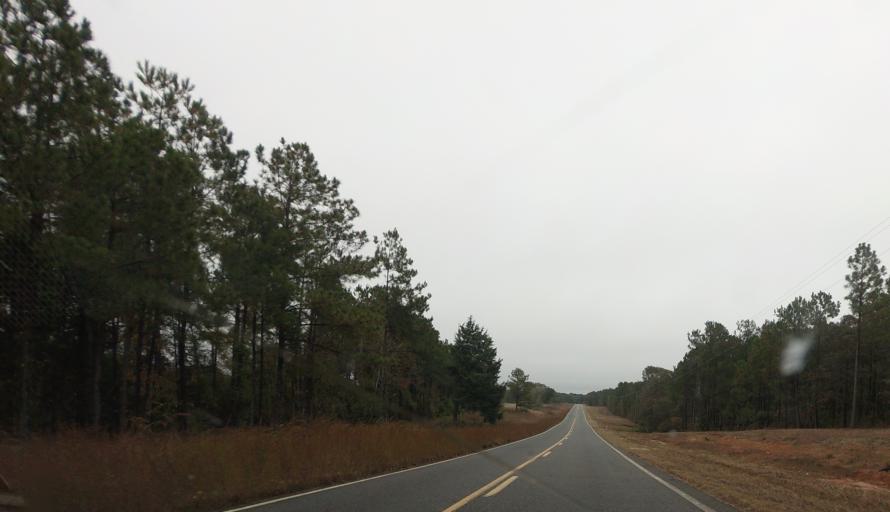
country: US
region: Georgia
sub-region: Taylor County
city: Butler
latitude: 32.4348
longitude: -84.3277
